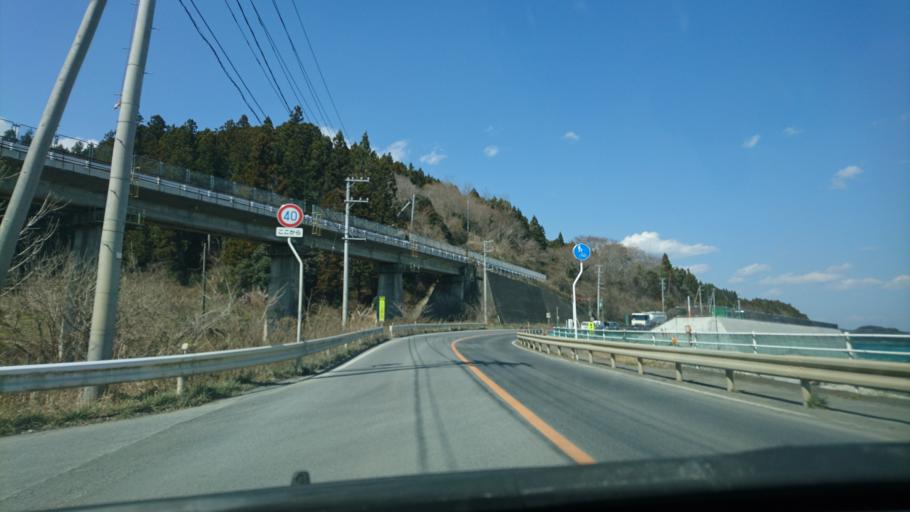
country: JP
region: Miyagi
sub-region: Oshika Gun
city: Onagawa Cho
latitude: 38.6506
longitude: 141.4431
